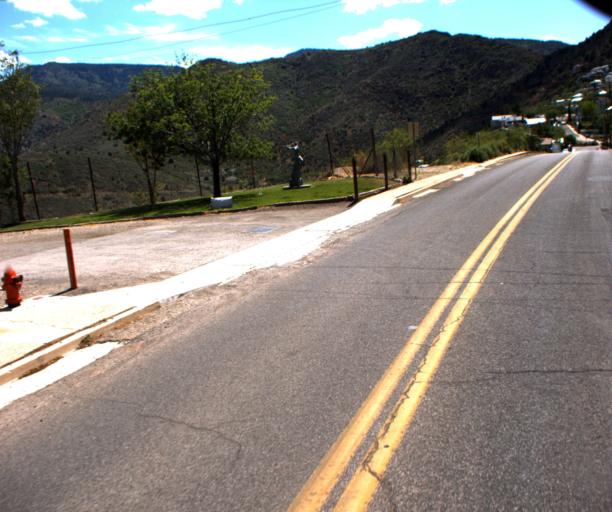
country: US
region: Arizona
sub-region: Yavapai County
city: Clarkdale
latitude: 34.7505
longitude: -112.1068
